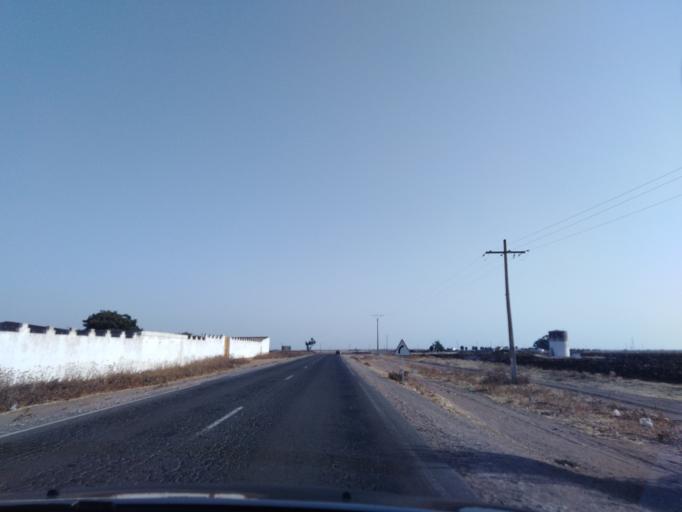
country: MA
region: Doukkala-Abda
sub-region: Safi
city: Youssoufia
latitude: 32.4716
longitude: -8.7730
